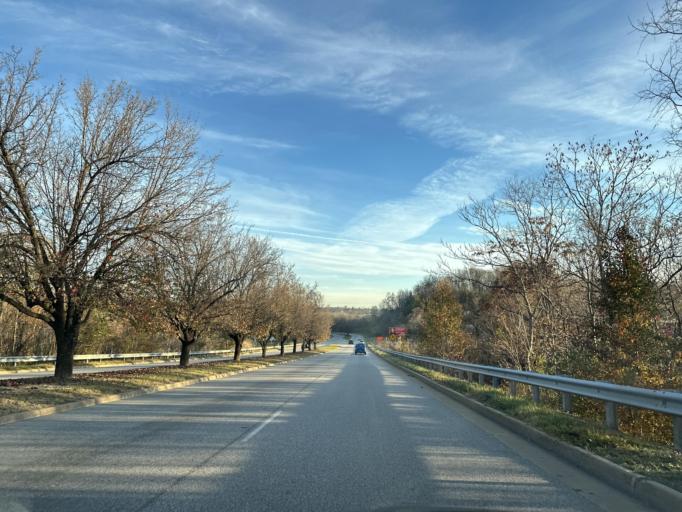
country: US
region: Virginia
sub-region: City of Staunton
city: Staunton
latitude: 38.1461
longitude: -79.0546
